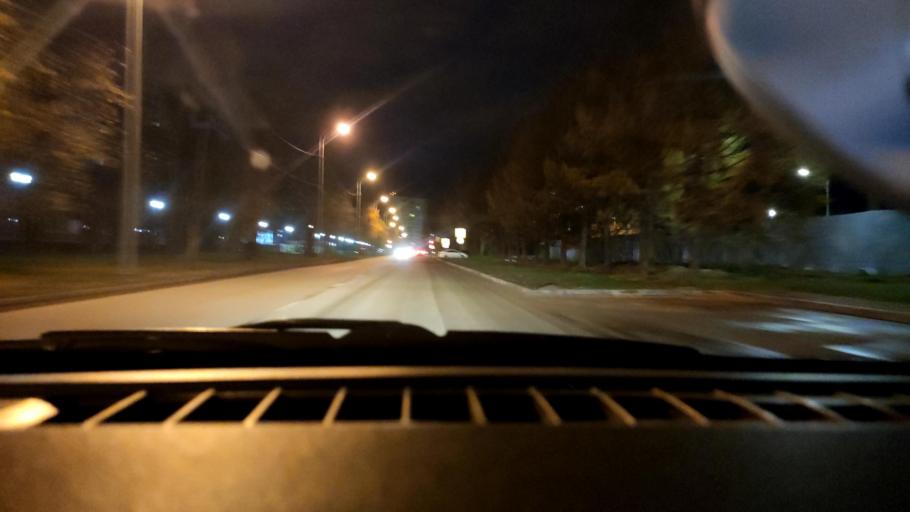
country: RU
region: Perm
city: Perm
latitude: 57.9627
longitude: 56.1858
